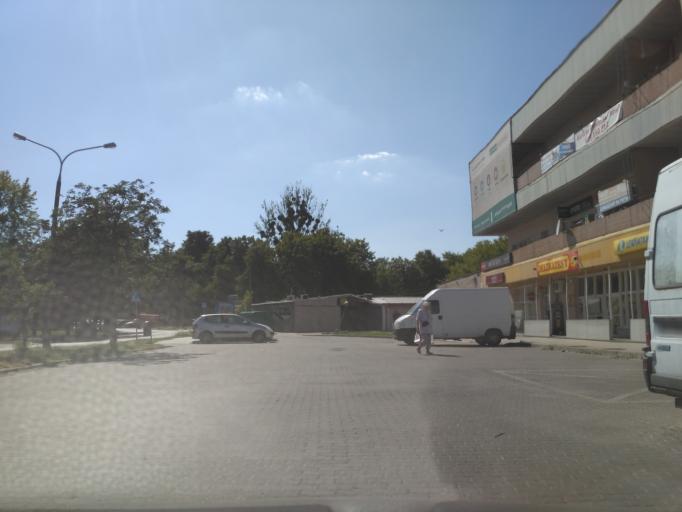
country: PL
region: Lublin Voivodeship
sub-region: Powiat lubelski
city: Lublin
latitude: 51.2629
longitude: 22.5454
